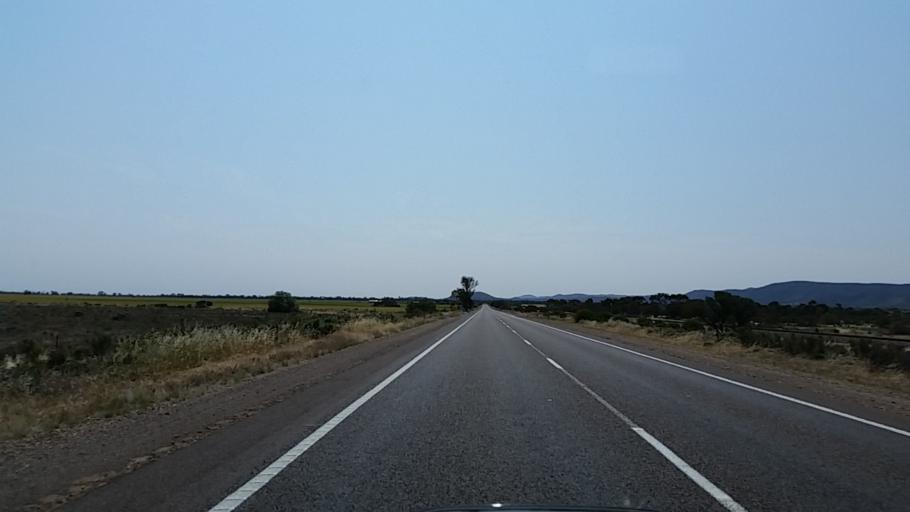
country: AU
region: South Australia
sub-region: Port Pirie City and Dists
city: Port Pirie
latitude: -32.8909
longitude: 137.9823
